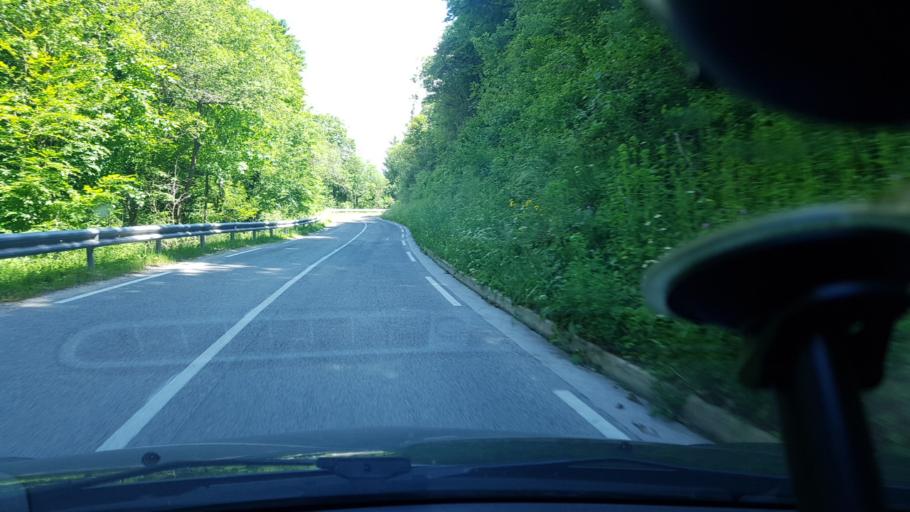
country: SI
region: Zrece
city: Zrece
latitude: 46.4095
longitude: 15.3630
